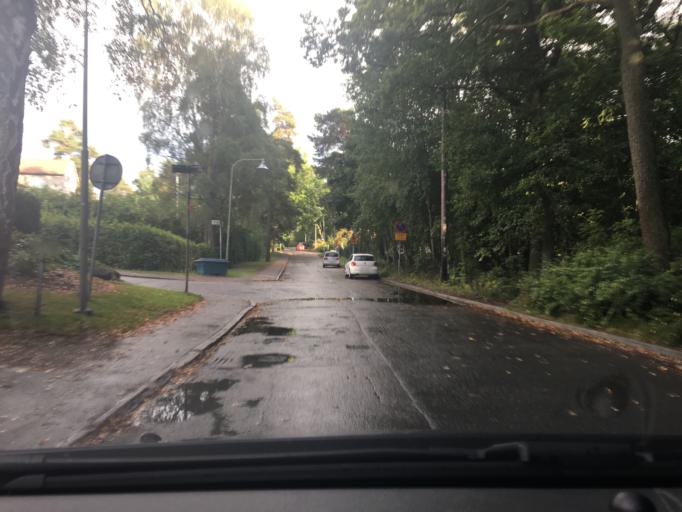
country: SE
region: Stockholm
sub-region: Stockholms Kommun
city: Bromma
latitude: 59.3307
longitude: 17.9631
